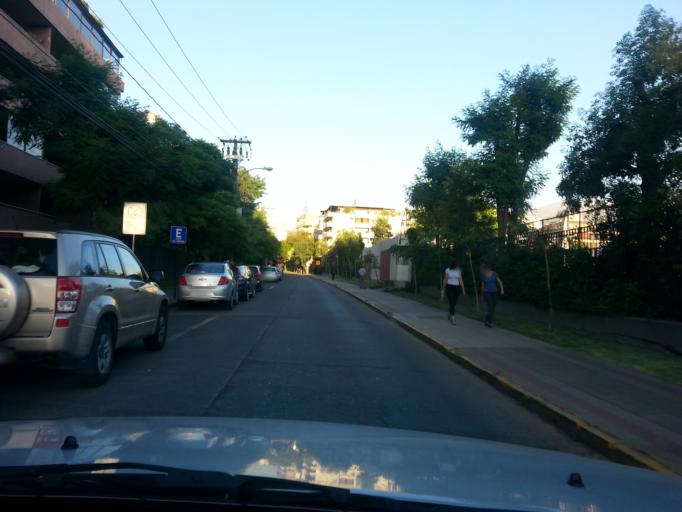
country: CL
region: Santiago Metropolitan
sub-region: Provincia de Santiago
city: Villa Presidente Frei, Nunoa, Santiago, Chile
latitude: -33.4305
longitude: -70.5932
